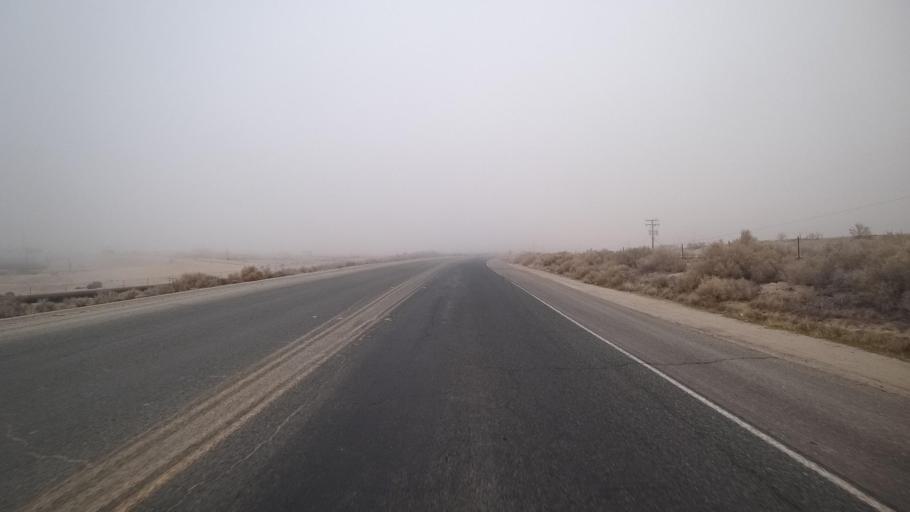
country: US
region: California
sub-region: Kern County
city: Ford City
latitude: 35.2755
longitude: -119.4678
